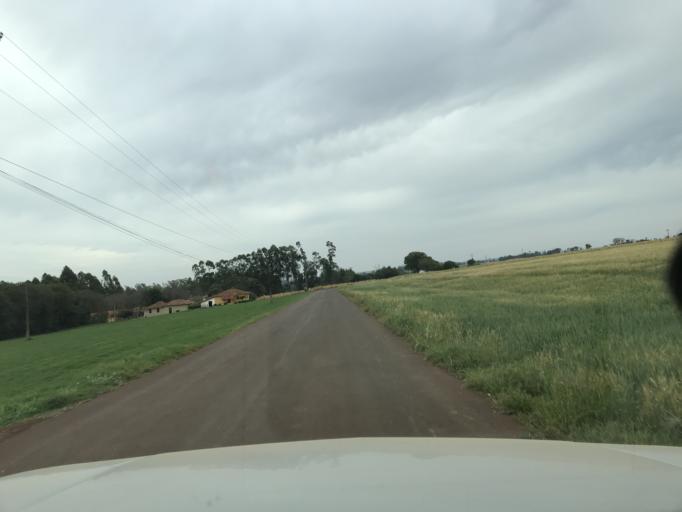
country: BR
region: Parana
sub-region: Marechal Candido Rondon
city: Marechal Candido Rondon
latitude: -24.4633
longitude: -53.9652
